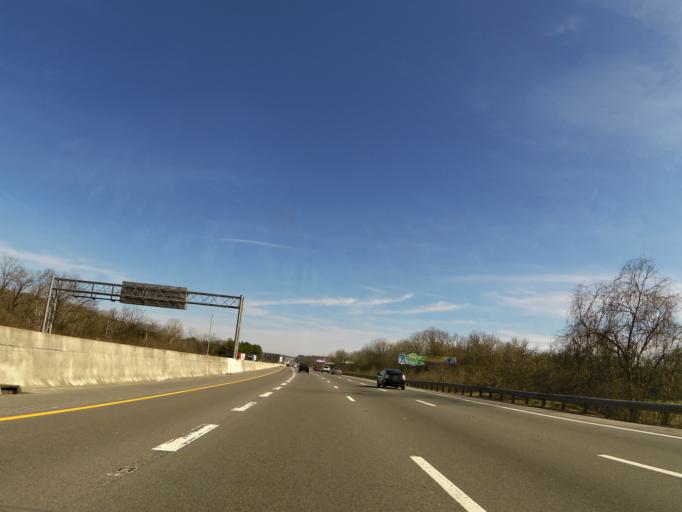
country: US
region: Tennessee
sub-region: Rutherford County
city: La Vergne
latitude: 36.0529
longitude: -86.6720
